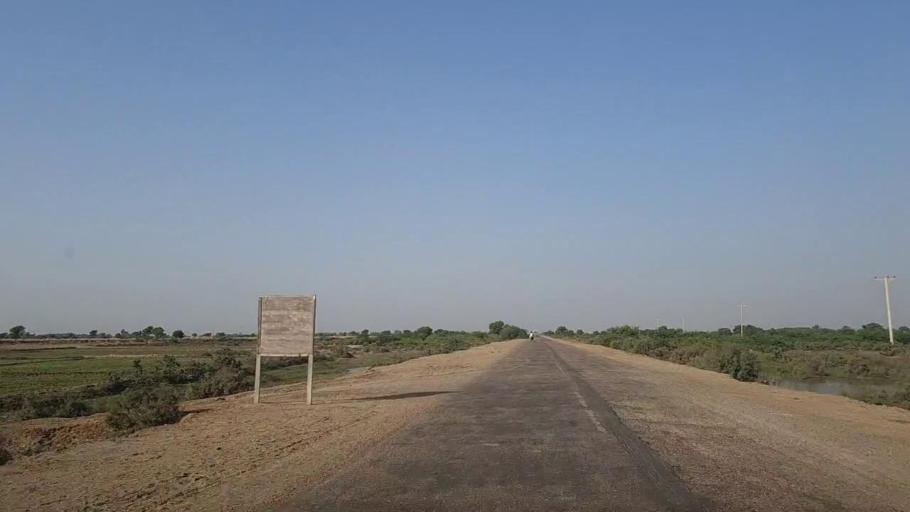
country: PK
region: Sindh
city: Mirpur Batoro
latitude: 24.6193
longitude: 68.4059
